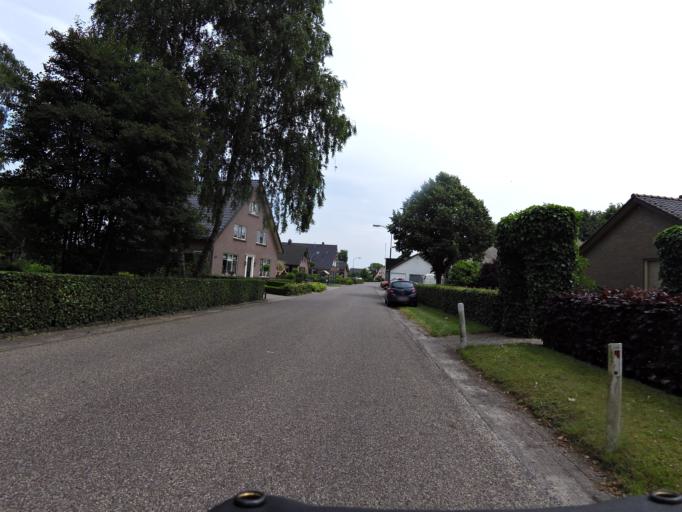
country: NL
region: Gelderland
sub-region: Gemeente Apeldoorn
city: Beekbergen
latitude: 52.1618
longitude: 5.9901
